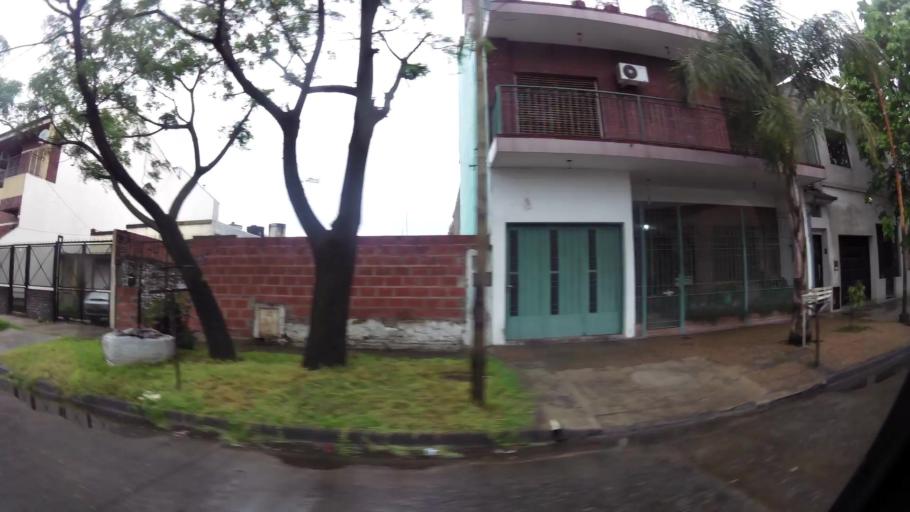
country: AR
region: Buenos Aires
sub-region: Partido de Lomas de Zamora
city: Lomas de Zamora
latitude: -34.7441
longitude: -58.3772
